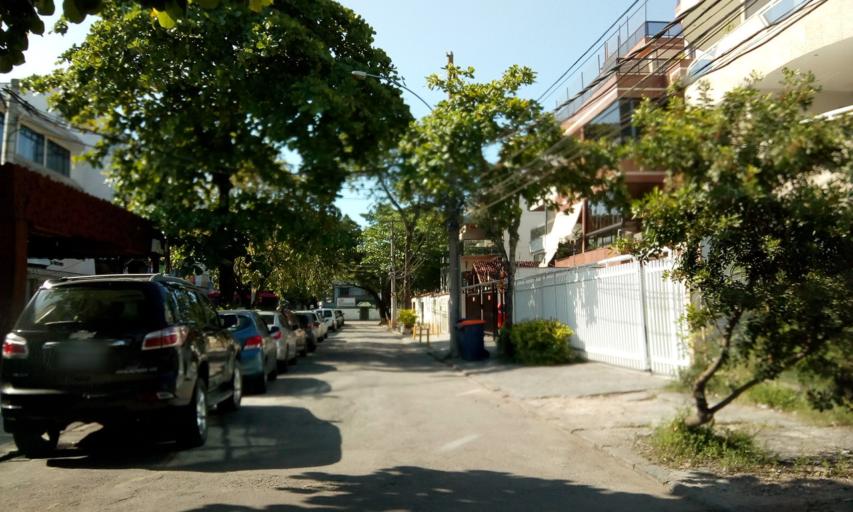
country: BR
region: Rio de Janeiro
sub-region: Nilopolis
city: Nilopolis
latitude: -23.0170
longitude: -43.4595
